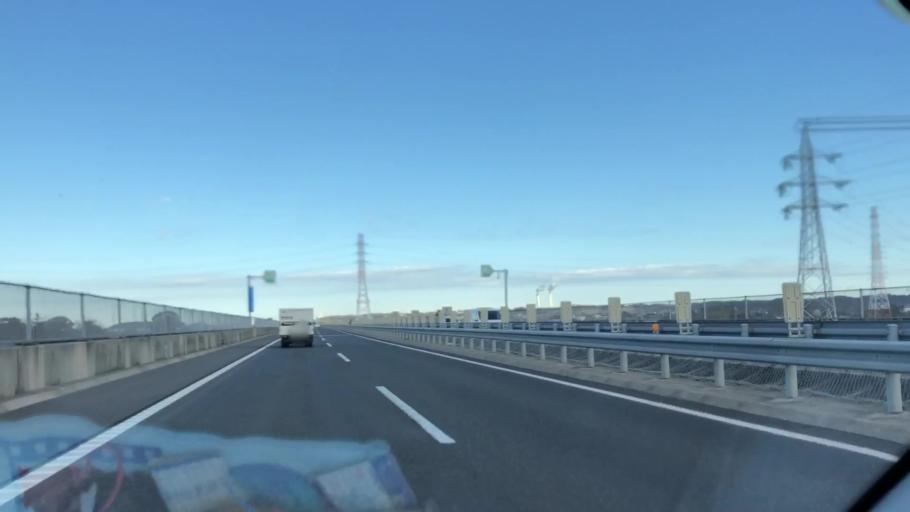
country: JP
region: Chiba
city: Kisarazu
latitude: 35.3955
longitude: 139.9684
